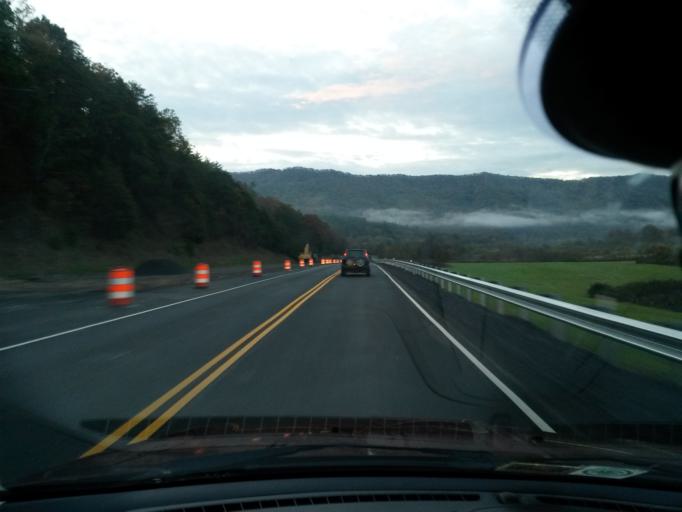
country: US
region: Virginia
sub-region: Alleghany County
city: Clifton Forge
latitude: 37.6763
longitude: -79.7994
